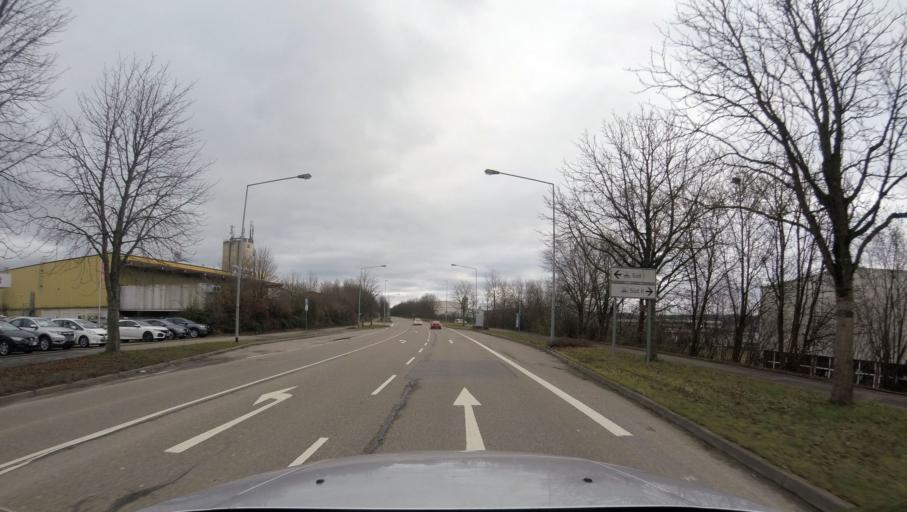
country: DE
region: Baden-Wuerttemberg
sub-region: Regierungsbezirk Stuttgart
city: Backnang
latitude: 48.9321
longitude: 9.4403
